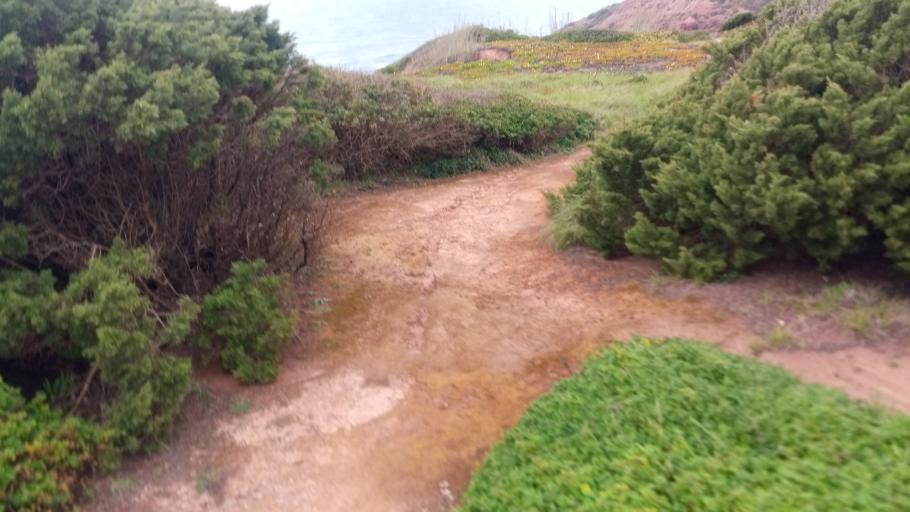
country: PT
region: Leiria
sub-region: Caldas da Rainha
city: Caldas da Rainha
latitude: 39.4872
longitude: -9.1815
